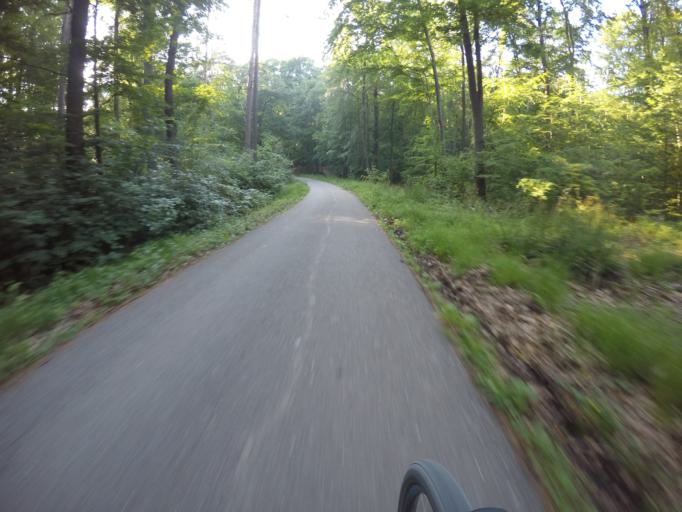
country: DE
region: Baden-Wuerttemberg
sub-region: Regierungsbezirk Stuttgart
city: Fellbach
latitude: 48.7879
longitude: 9.2969
